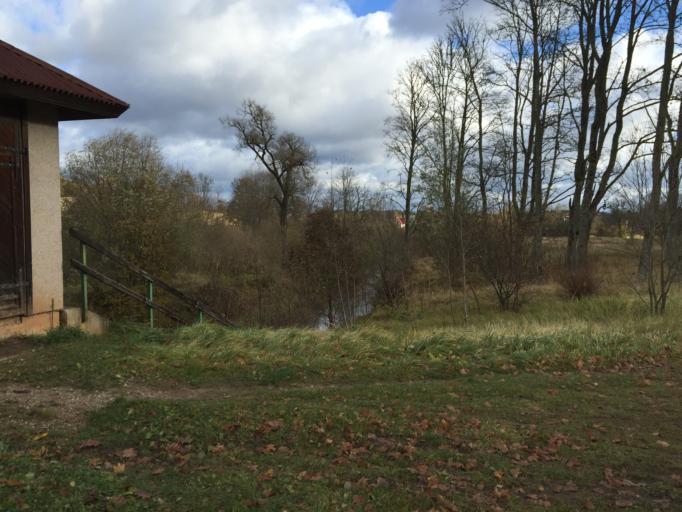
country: LV
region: Tukuma Rajons
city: Tukums
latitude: 56.9738
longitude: 23.2087
